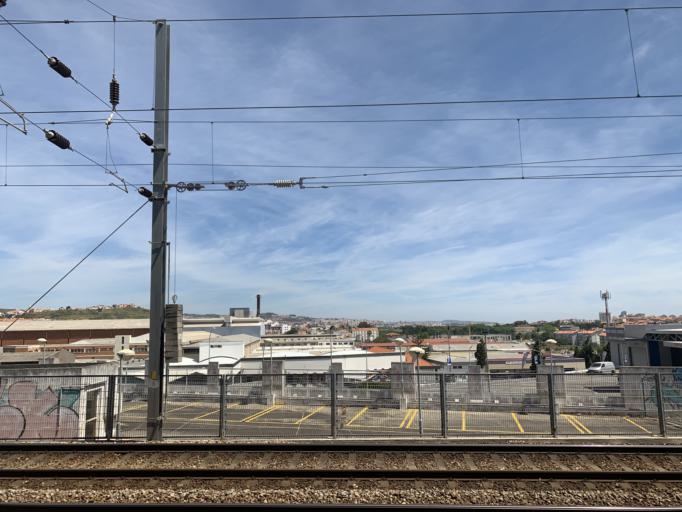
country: PT
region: Lisbon
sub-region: Amadora
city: Amadora
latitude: 38.7504
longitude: -9.2207
